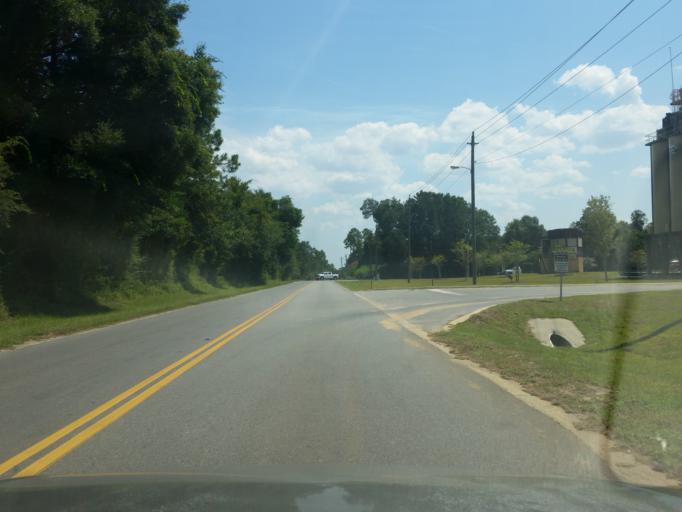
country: US
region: Florida
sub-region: Escambia County
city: Cantonment
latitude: 30.6122
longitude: -87.3191
